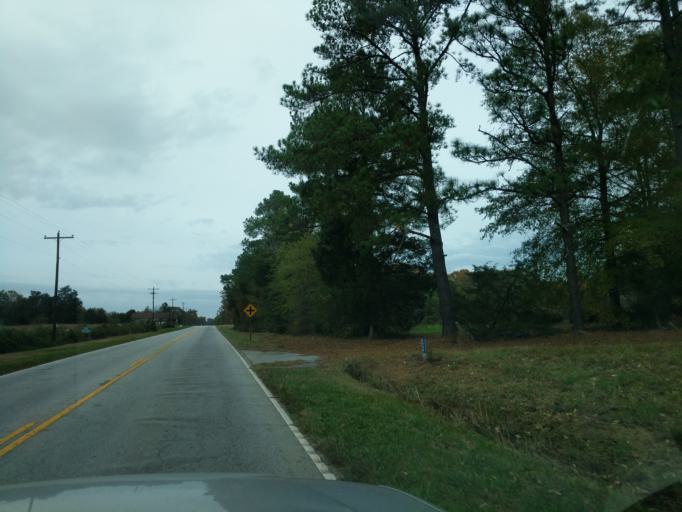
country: US
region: South Carolina
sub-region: Saluda County
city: Saluda
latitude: 34.1247
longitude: -81.7480
